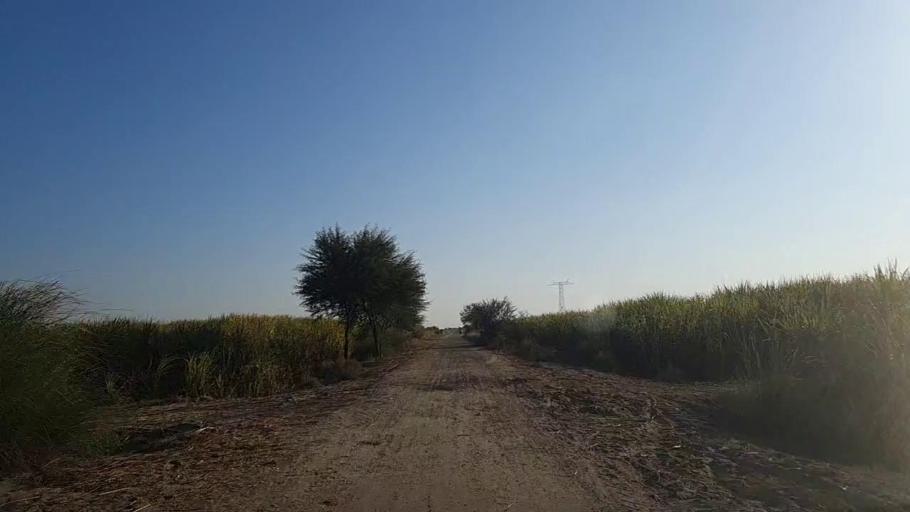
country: PK
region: Sindh
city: Khadro
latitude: 26.2691
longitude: 68.8603
